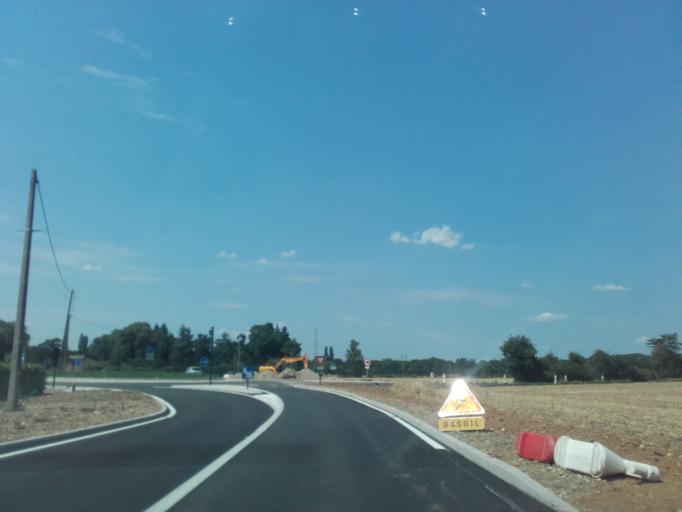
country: FR
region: Rhone-Alpes
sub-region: Departement de l'Isere
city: Cremieu
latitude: 45.7325
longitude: 5.2357
